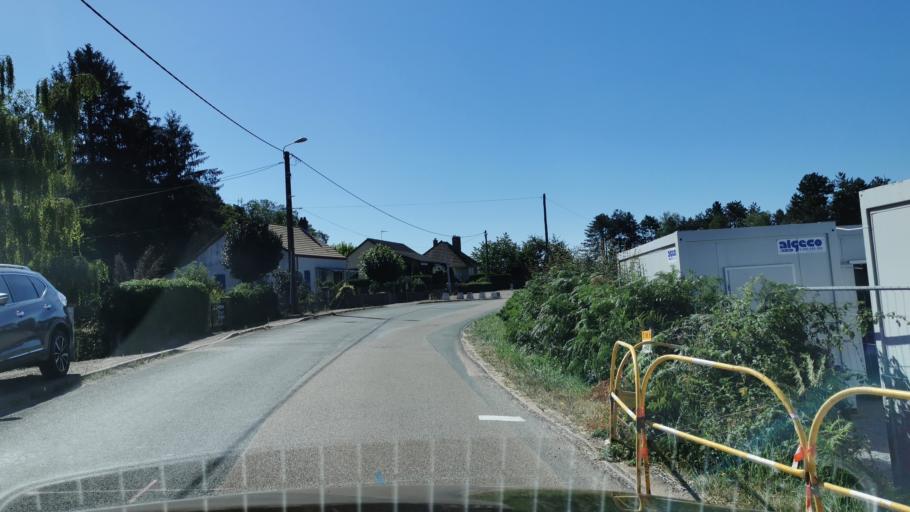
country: FR
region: Bourgogne
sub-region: Departement de Saone-et-Loire
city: Saint-Leu
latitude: 46.7506
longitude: 4.4935
